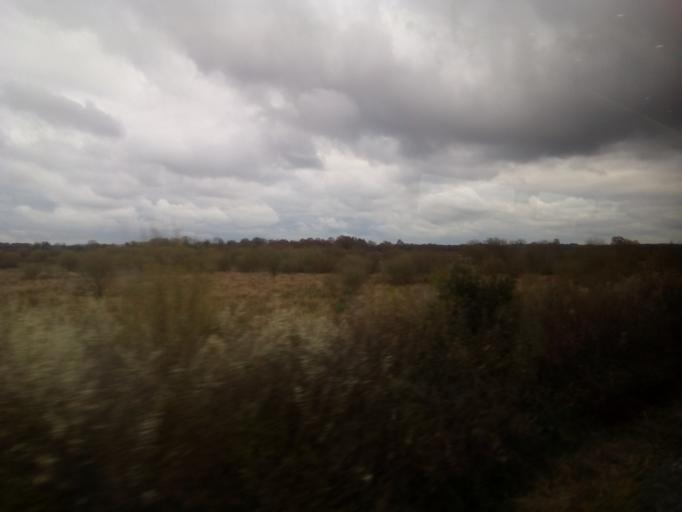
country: IE
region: Leinster
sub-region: An Longfort
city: Longford
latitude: 53.8114
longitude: -7.8667
